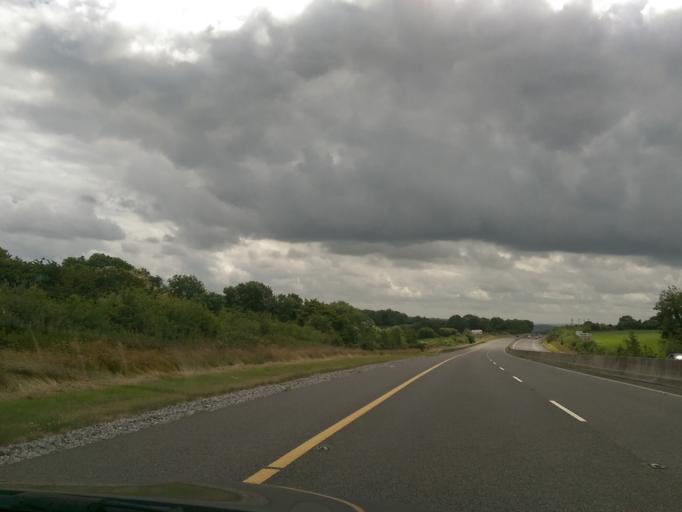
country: IE
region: Munster
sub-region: County Cork
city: Mitchelstown
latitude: 52.2077
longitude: -8.2749
